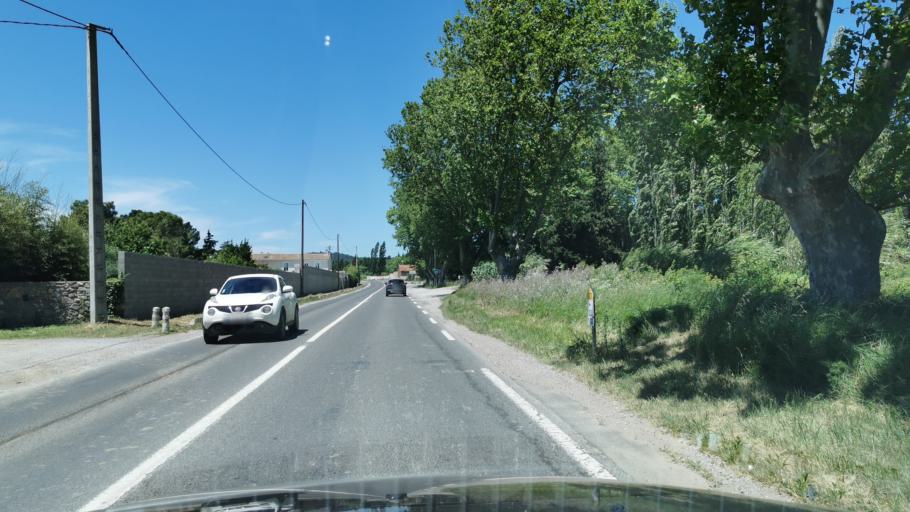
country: FR
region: Languedoc-Roussillon
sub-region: Departement de l'Aude
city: Narbonne
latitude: 43.1950
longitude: 2.9789
